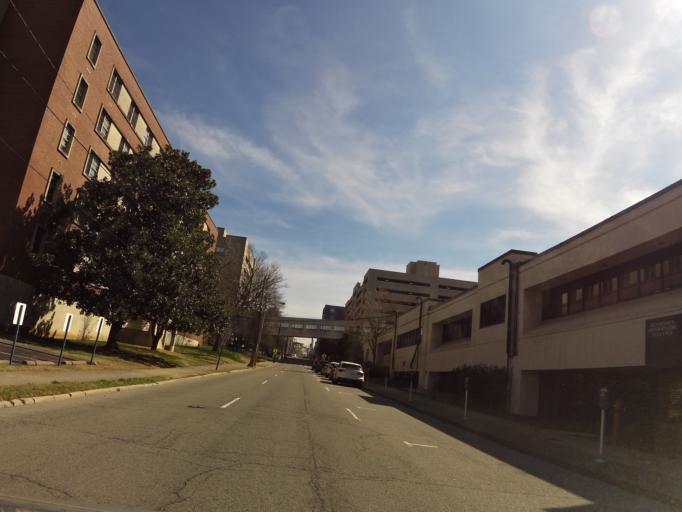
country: US
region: Tennessee
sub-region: Davidson County
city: Nashville
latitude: 36.1543
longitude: -86.8041
